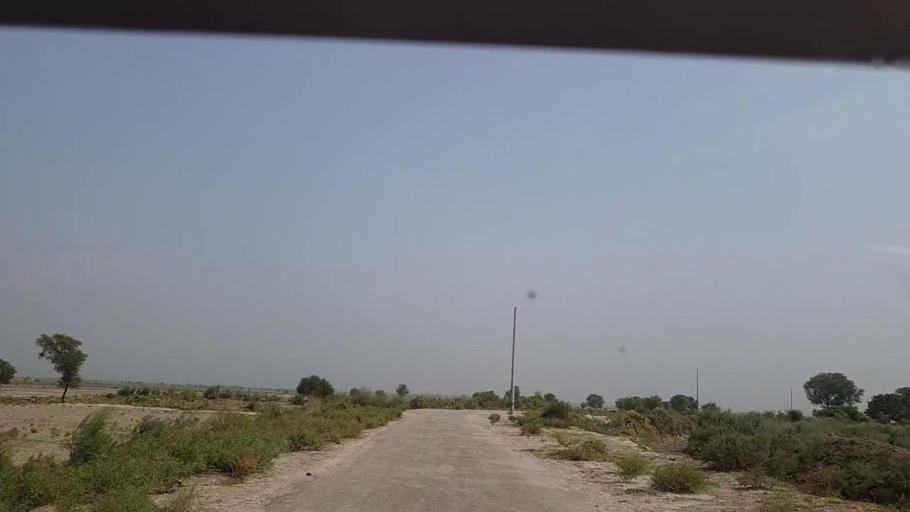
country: PK
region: Sindh
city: Khairpur Nathan Shah
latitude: 27.0448
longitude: 67.6863
